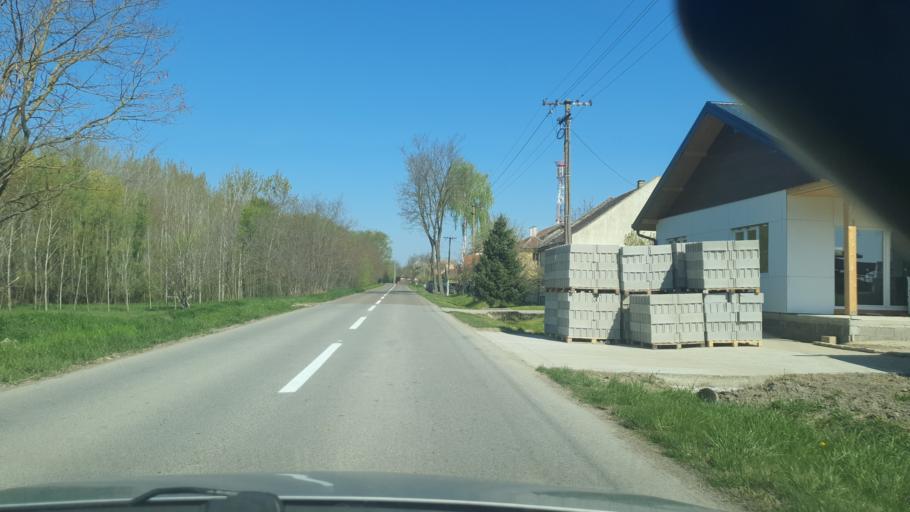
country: RS
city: Kolut
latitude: 45.8818
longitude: 18.9333
